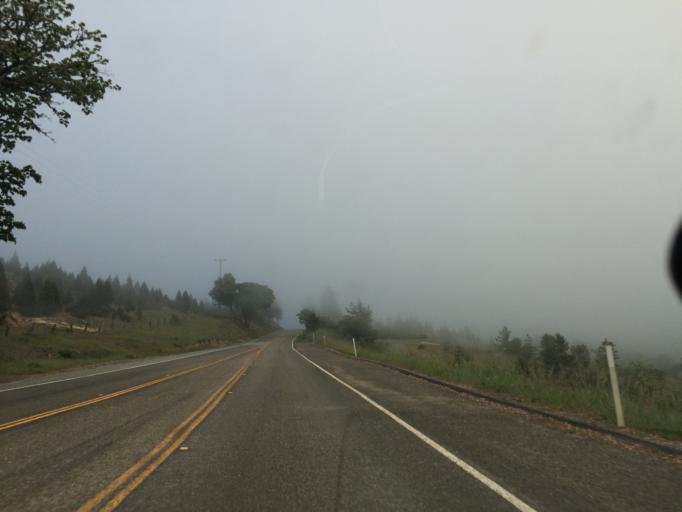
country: US
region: California
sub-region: Santa Clara County
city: Los Altos Hills
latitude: 37.3114
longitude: -122.1729
